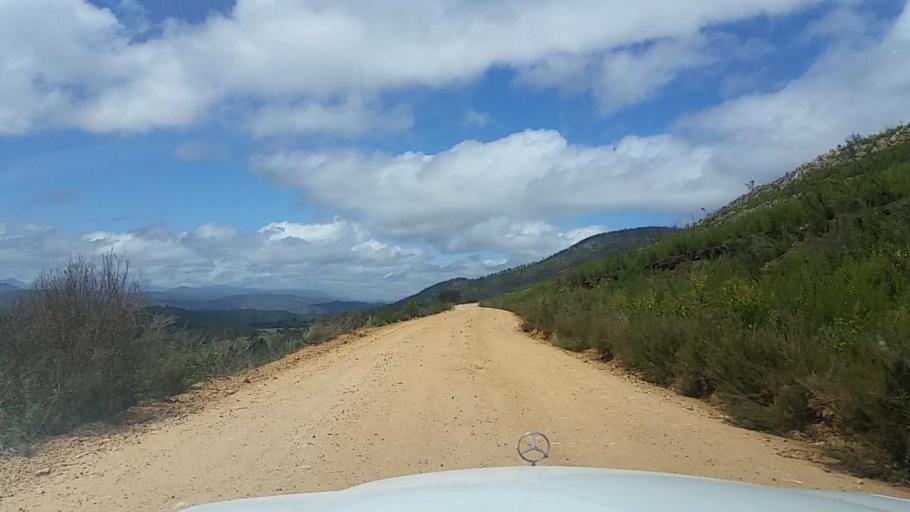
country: ZA
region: Western Cape
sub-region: Eden District Municipality
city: Knysna
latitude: -33.8896
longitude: 23.1695
